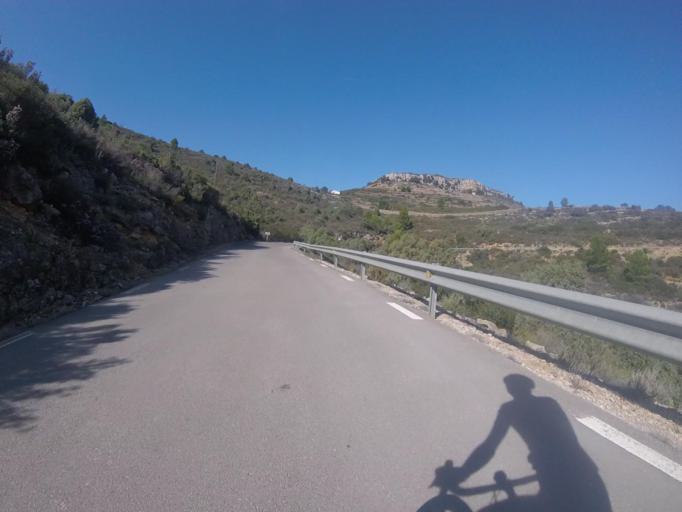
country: ES
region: Valencia
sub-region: Provincia de Castello
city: Sarratella
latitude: 40.2875
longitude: 0.0356
